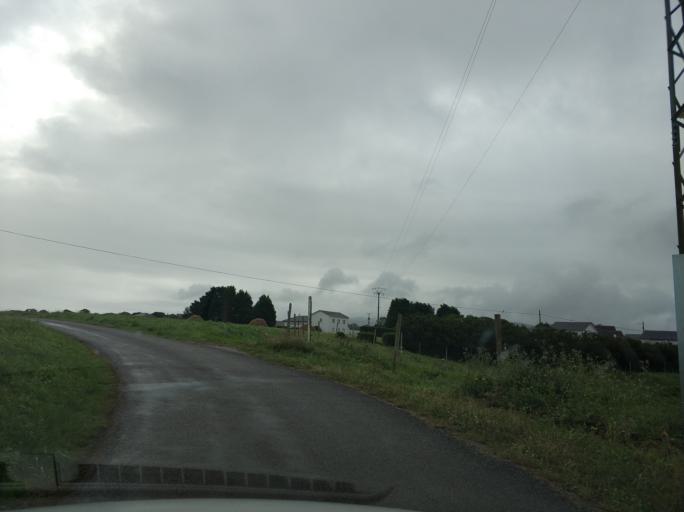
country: ES
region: Asturias
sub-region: Province of Asturias
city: Tineo
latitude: 43.5581
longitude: -6.4664
